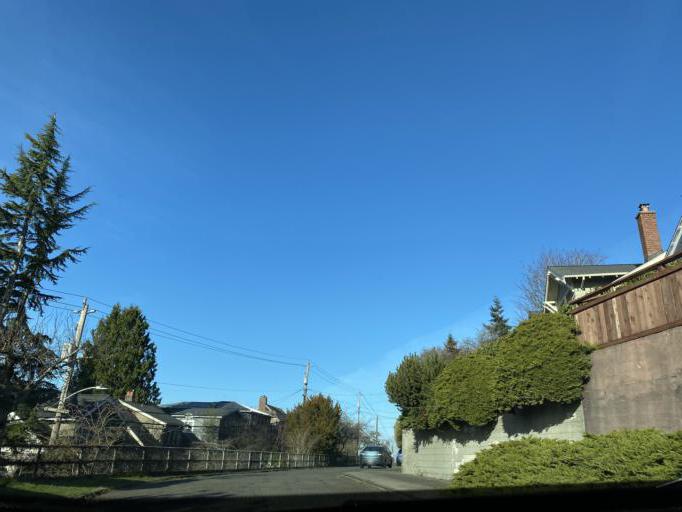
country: US
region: Washington
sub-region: King County
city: Seattle
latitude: 47.6413
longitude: -122.3714
